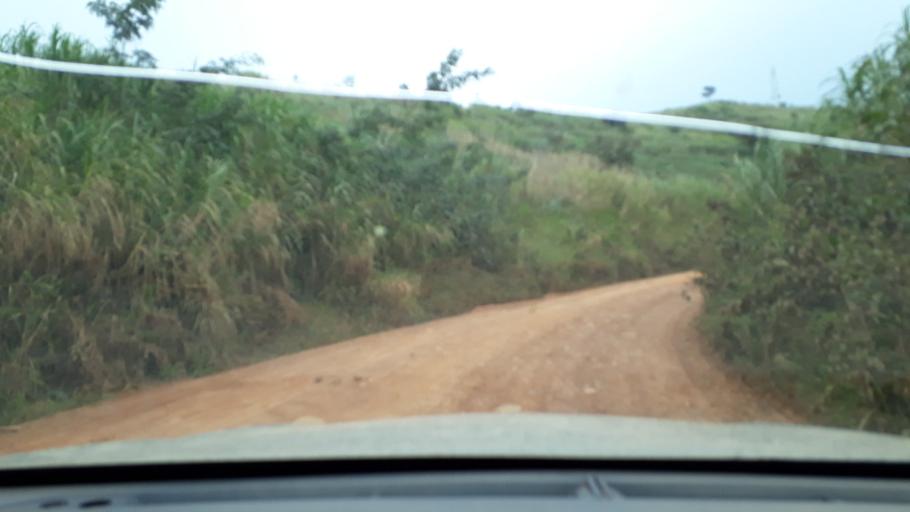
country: CD
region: Eastern Province
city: Bunia
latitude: 1.8195
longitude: 30.4357
